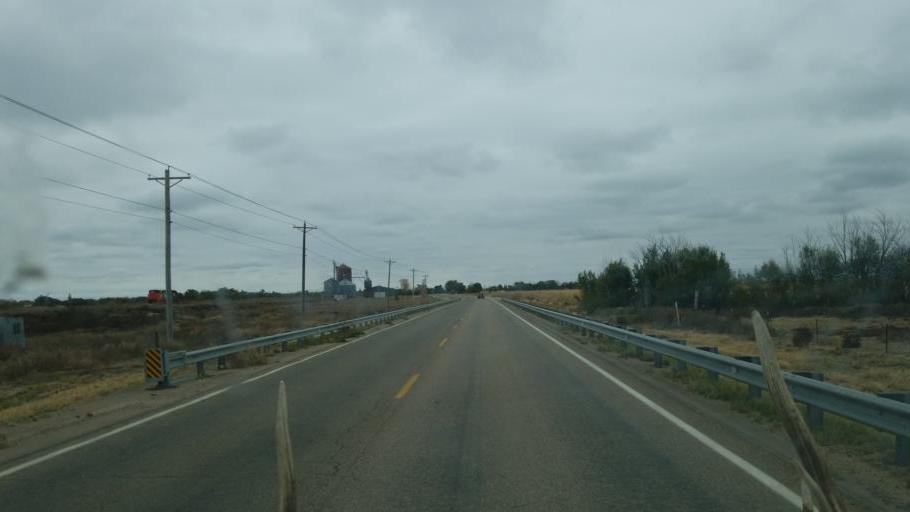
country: US
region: Colorado
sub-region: Crowley County
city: Ordway
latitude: 38.2109
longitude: -103.7755
